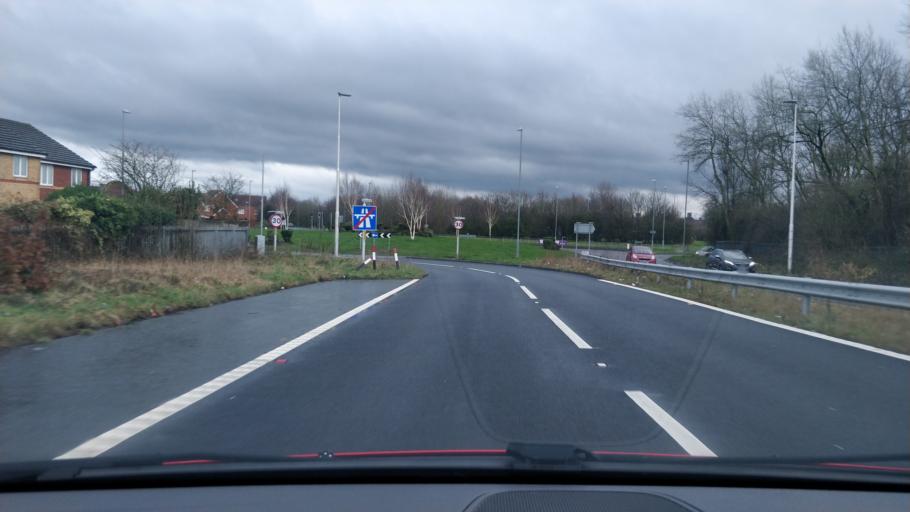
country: GB
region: England
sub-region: Knowsley
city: Knowsley
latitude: 53.4303
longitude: -2.8559
